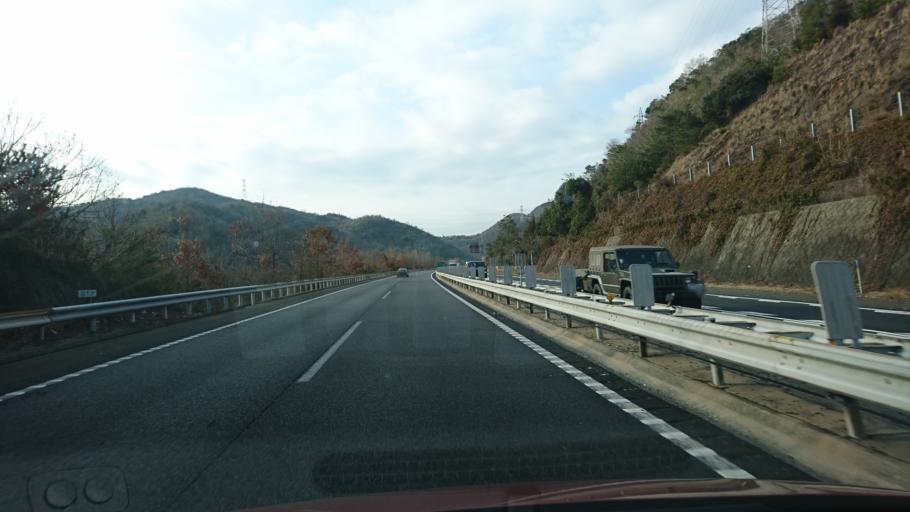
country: JP
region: Hyogo
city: Aioi
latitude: 34.7989
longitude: 134.4352
